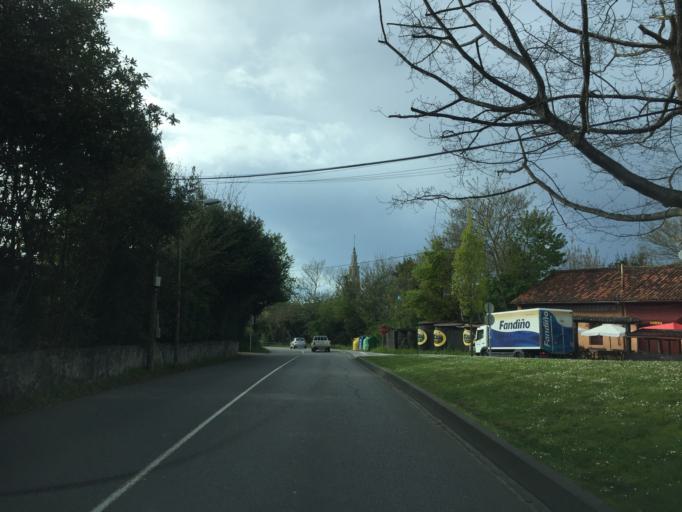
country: ES
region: Asturias
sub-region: Province of Asturias
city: Gijon
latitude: 43.5194
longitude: -5.6080
